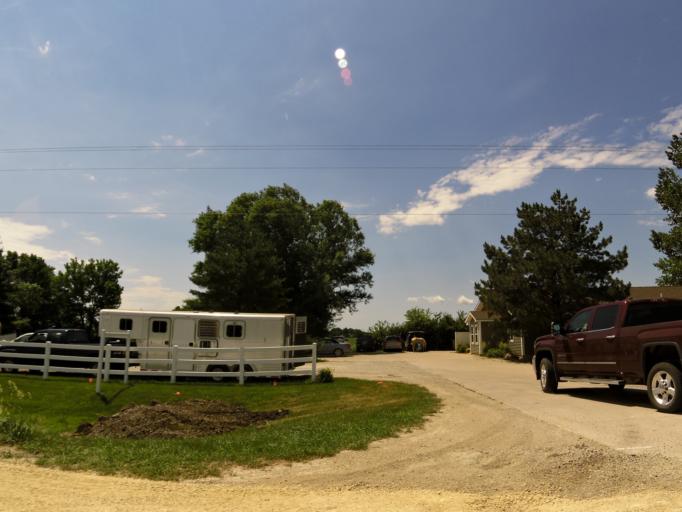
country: US
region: Iowa
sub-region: Bremer County
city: Tripoli
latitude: 42.7150
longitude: -92.2305
